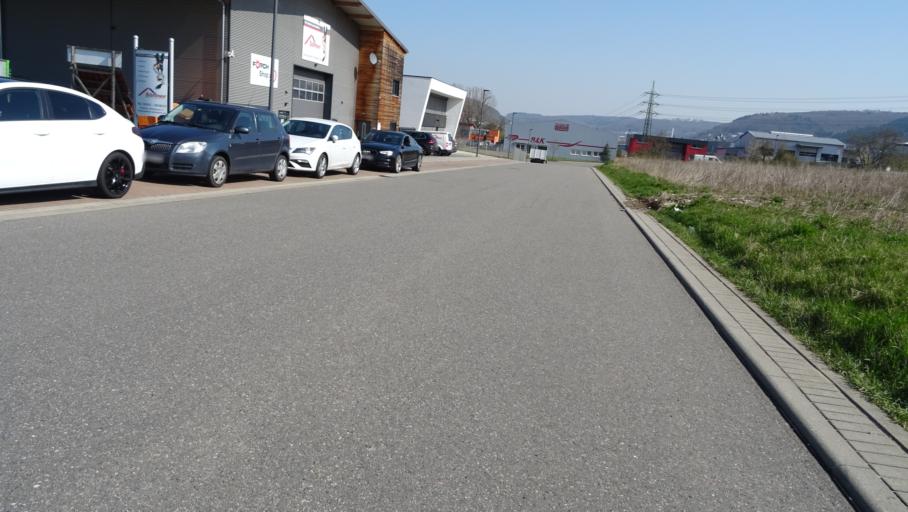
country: DE
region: Baden-Wuerttemberg
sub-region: Karlsruhe Region
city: Obrigheim
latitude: 49.3369
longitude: 9.1101
